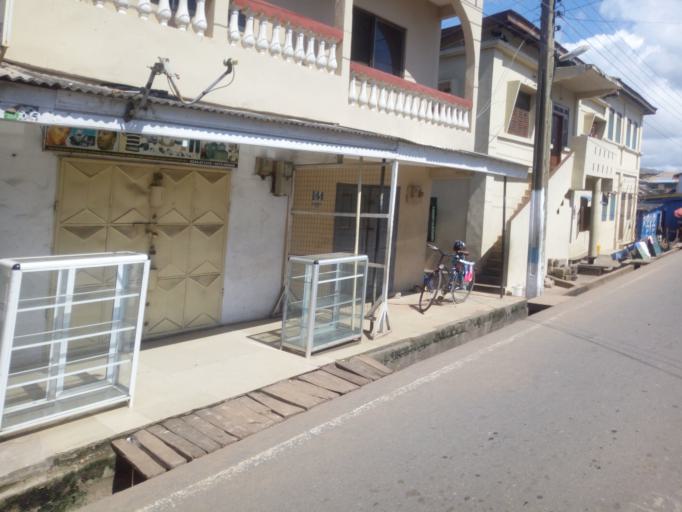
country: GH
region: Central
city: Elmina
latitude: 5.0868
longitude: -1.3494
